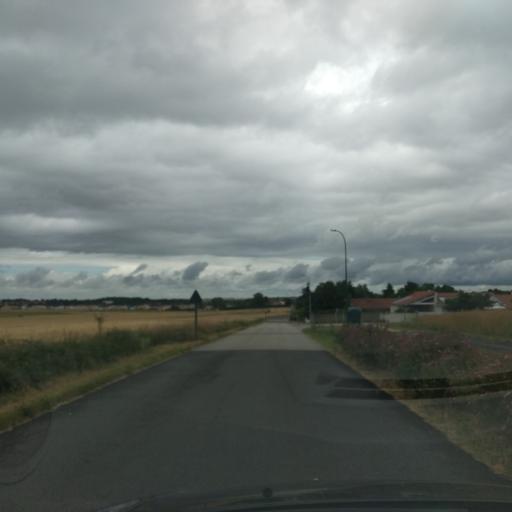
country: FR
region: Poitou-Charentes
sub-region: Departement de la Vienne
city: Vouneuil-sous-Biard
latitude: 46.5966
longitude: 0.2737
